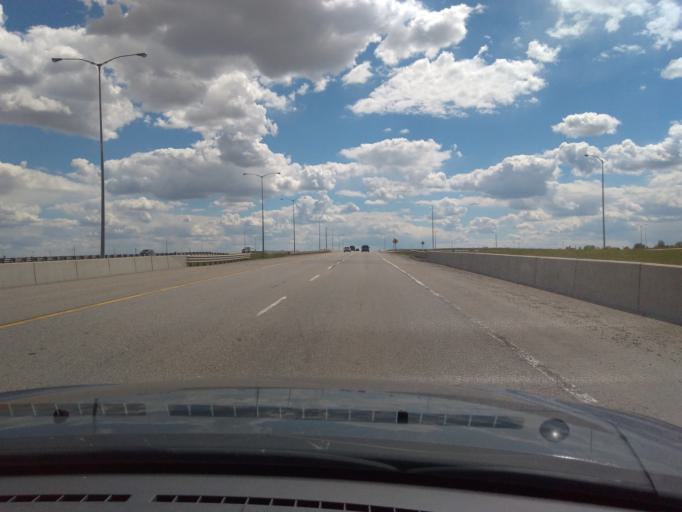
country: CA
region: Alberta
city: Chestermere
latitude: 51.0692
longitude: -113.9208
